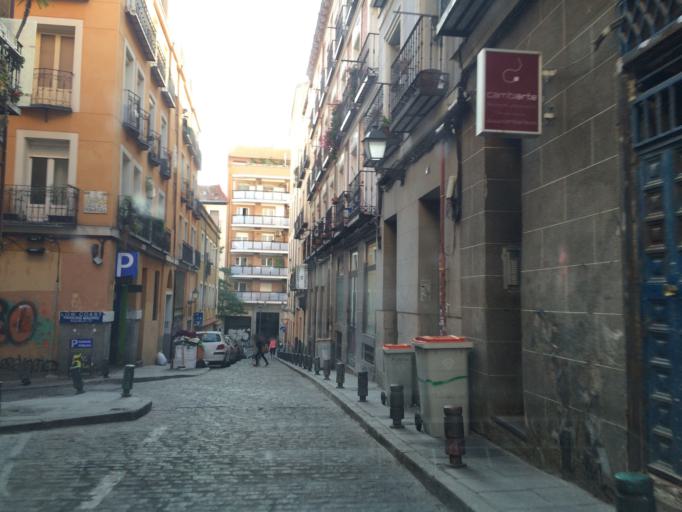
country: ES
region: Madrid
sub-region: Provincia de Madrid
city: Madrid
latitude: 40.4102
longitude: -3.7002
